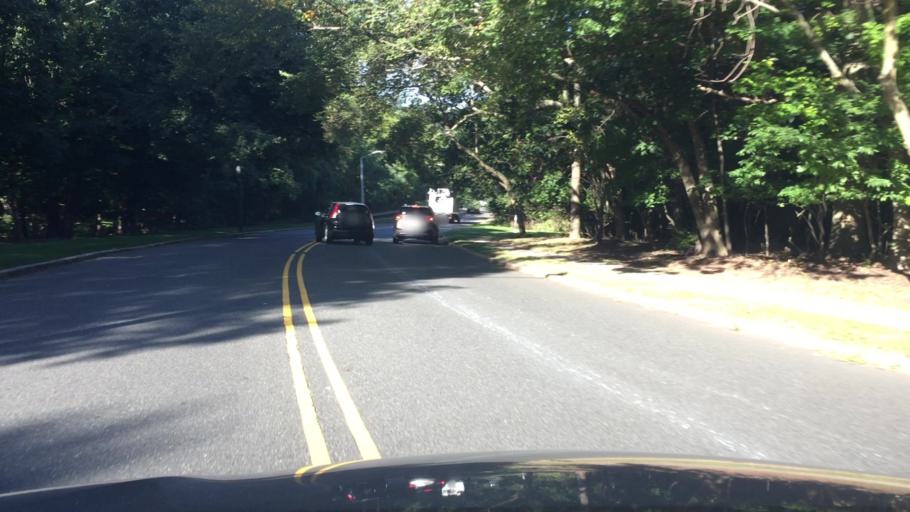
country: US
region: New Jersey
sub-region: Somerset County
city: Middlebush
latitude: 40.5178
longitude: -74.5102
